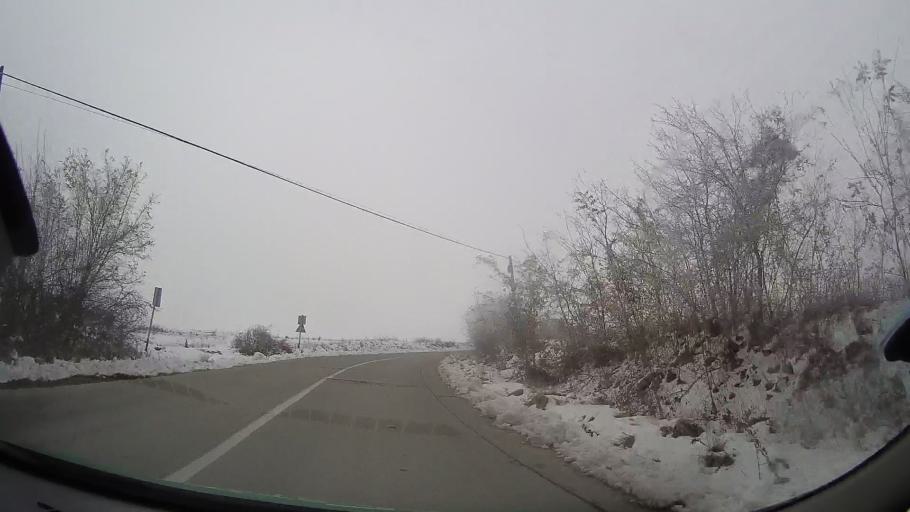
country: RO
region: Bacau
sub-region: Comuna Podu Turcului
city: Podu Turcului
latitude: 46.2040
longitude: 27.3941
